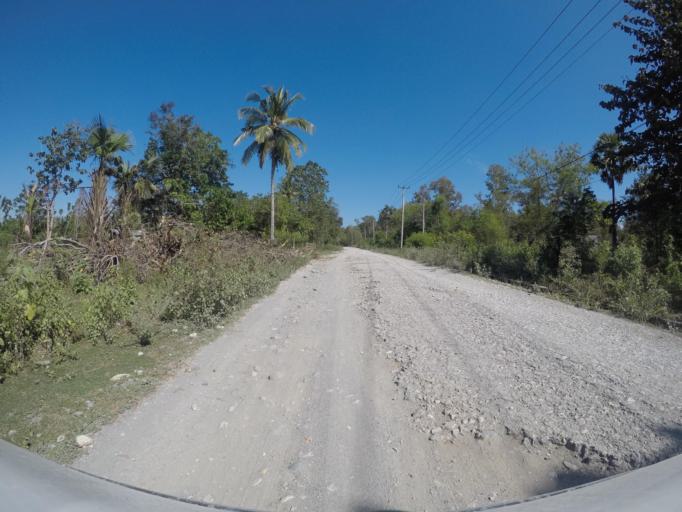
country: TL
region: Viqueque
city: Viqueque
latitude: -8.9728
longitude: 126.0609
